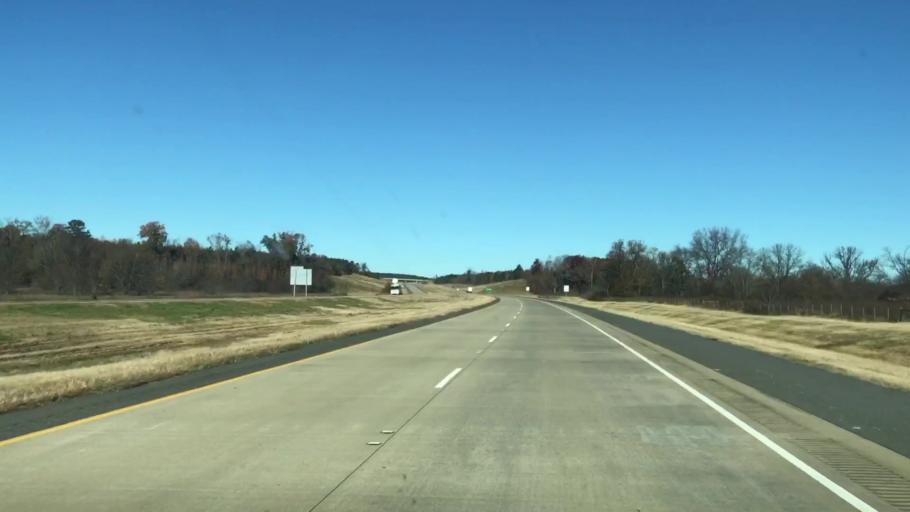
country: US
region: Louisiana
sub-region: Caddo Parish
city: Vivian
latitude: 32.9079
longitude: -93.8678
